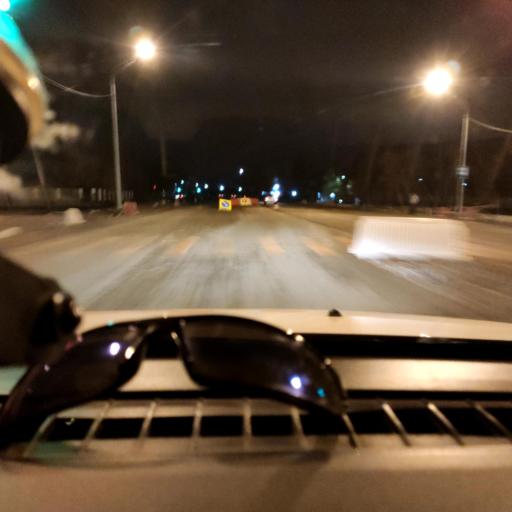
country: RU
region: Samara
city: Samara
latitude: 53.1330
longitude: 50.0981
